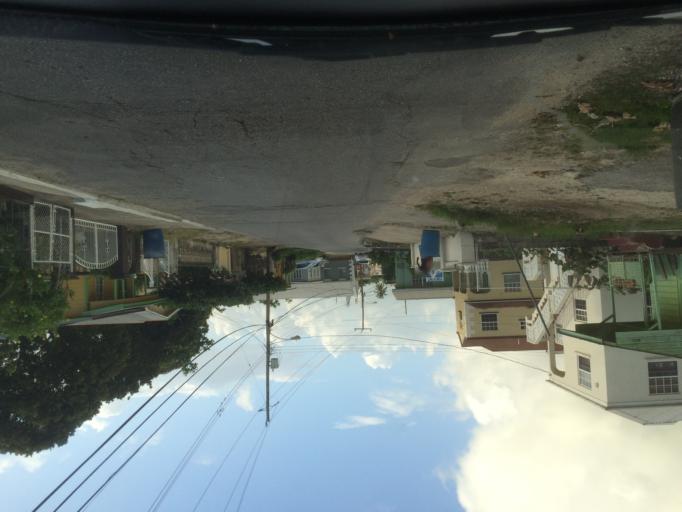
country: BB
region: Saint Lucy
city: Checker Hall
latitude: 13.2791
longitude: -59.6476
